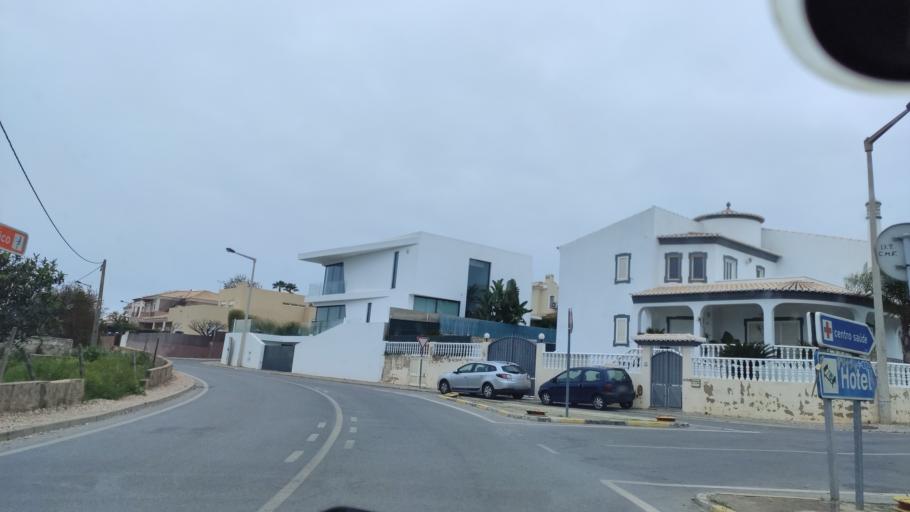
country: PT
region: Faro
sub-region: Faro
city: Faro
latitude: 37.0331
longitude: -7.9551
